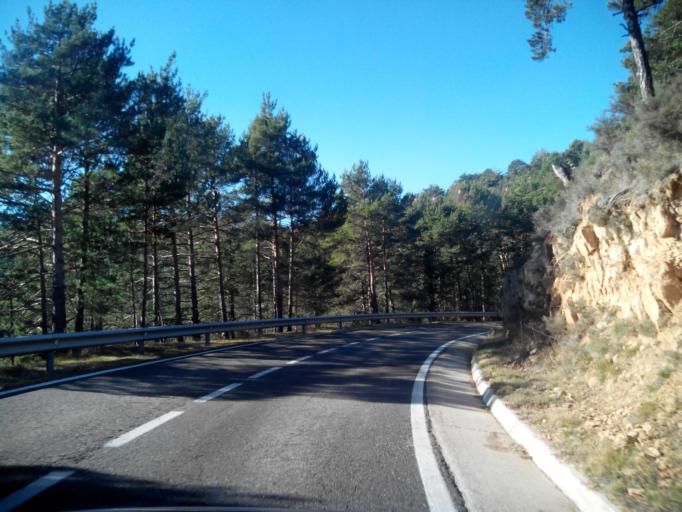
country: ES
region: Catalonia
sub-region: Provincia de Barcelona
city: Castellar del Riu
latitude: 42.0938
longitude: 1.7830
